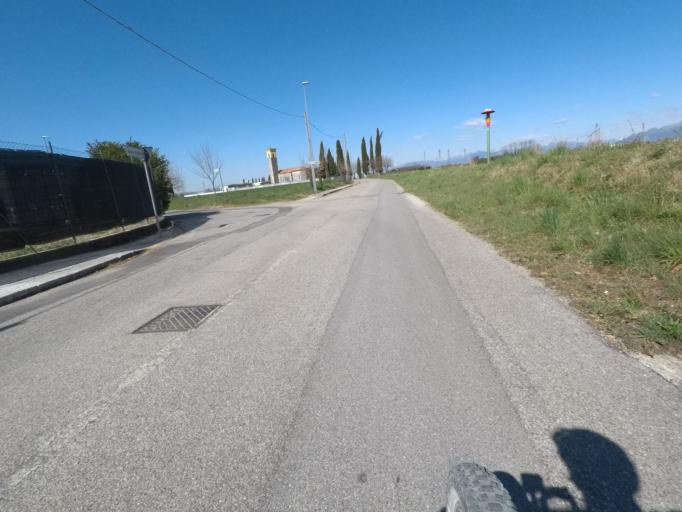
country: IT
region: Friuli Venezia Giulia
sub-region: Provincia di Udine
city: Remanzacco
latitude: 46.0869
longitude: 13.3159
